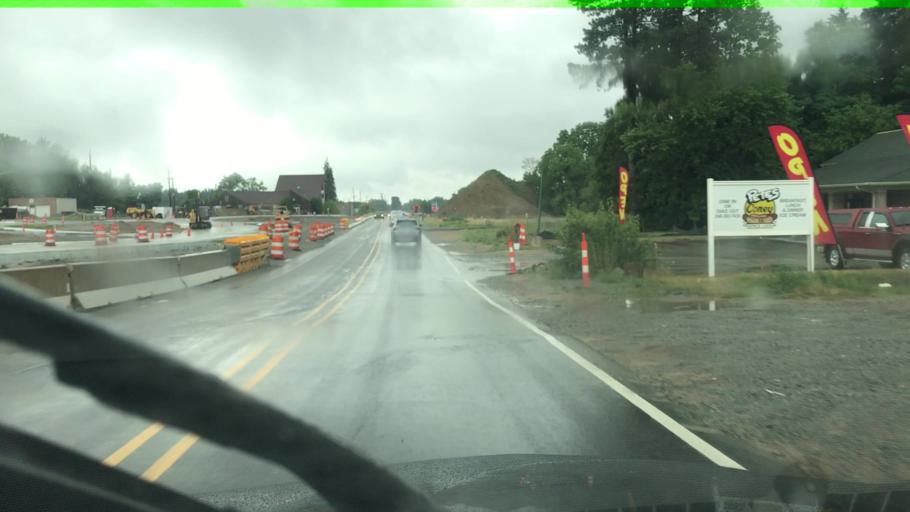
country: US
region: Michigan
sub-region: Oakland County
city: Auburn Hills
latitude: 42.7201
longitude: -83.3073
